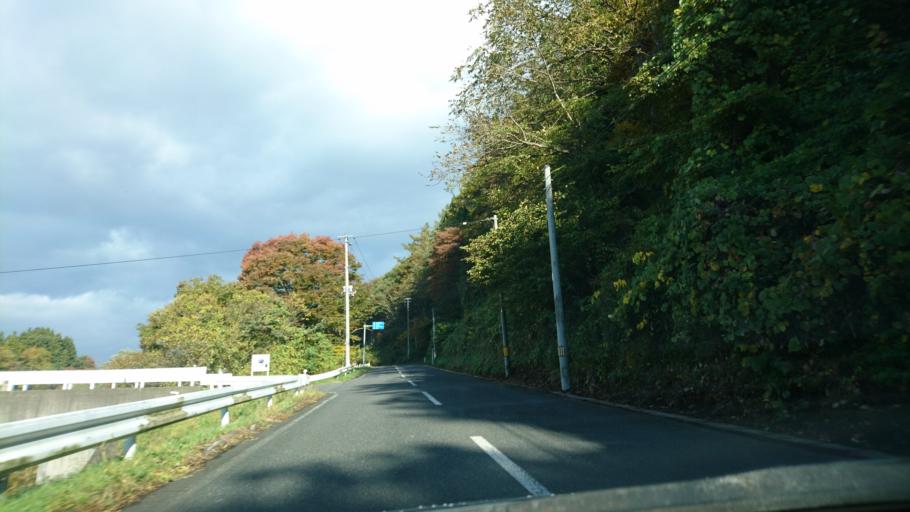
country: JP
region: Iwate
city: Mizusawa
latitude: 39.0682
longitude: 141.0262
